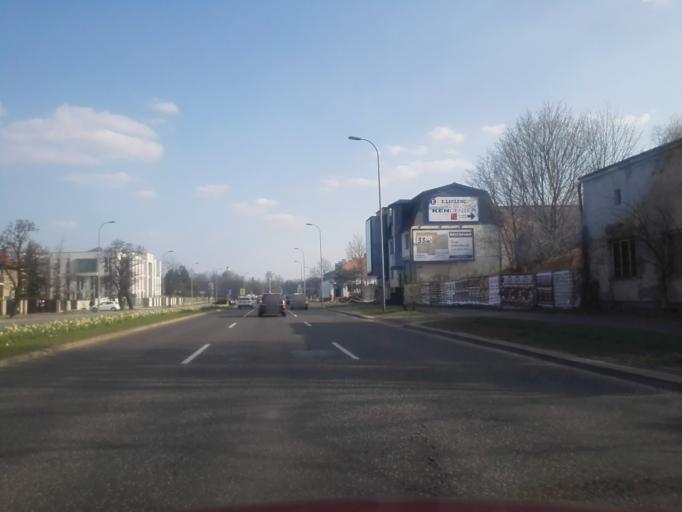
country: PL
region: Masovian Voivodeship
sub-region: Warszawa
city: Wilanow
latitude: 52.1704
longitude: 21.0826
